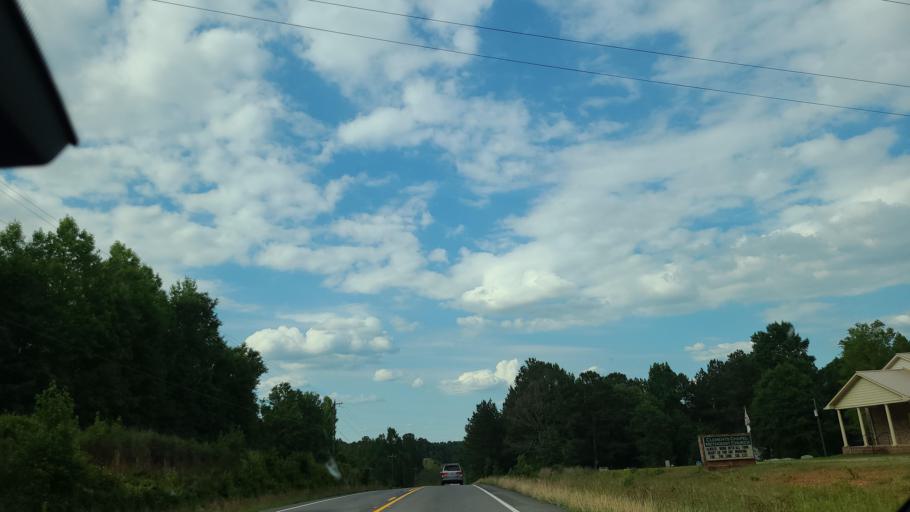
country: US
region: Georgia
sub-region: Putnam County
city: Eatonton
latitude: 33.2473
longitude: -83.4299
